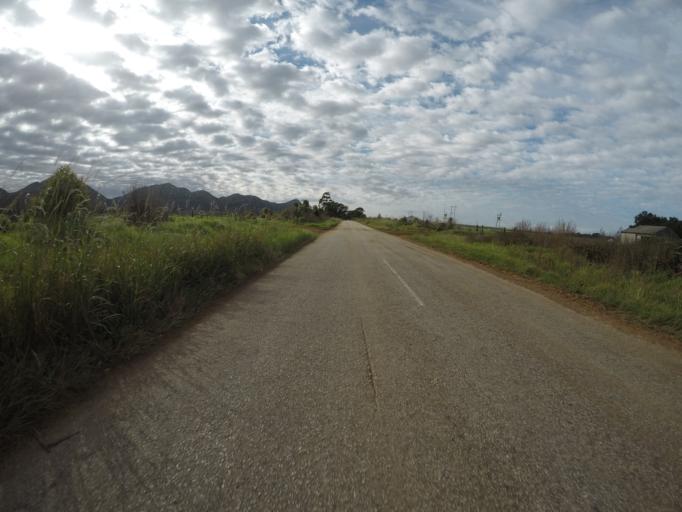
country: ZA
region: Eastern Cape
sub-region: Cacadu District Municipality
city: Kareedouw
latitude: -34.0452
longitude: 24.4443
